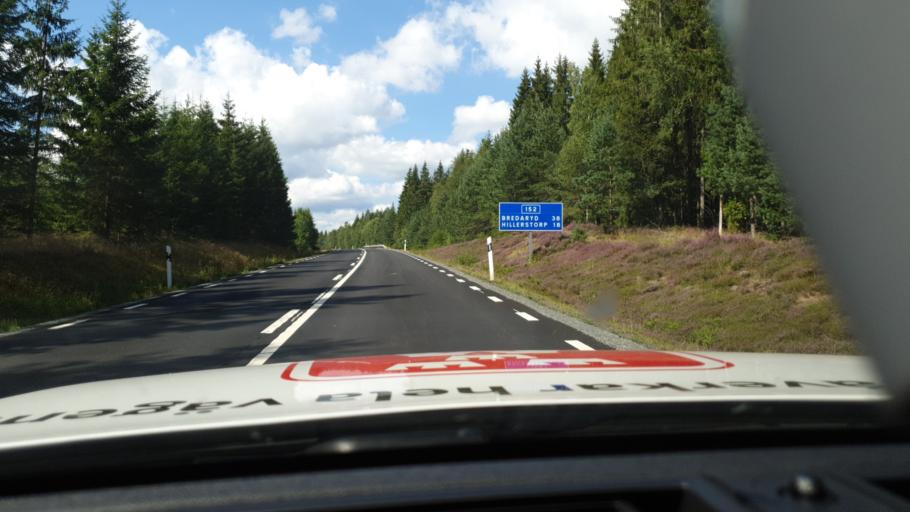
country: SE
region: Joenkoeping
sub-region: Vaggeryds Kommun
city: Skillingaryd
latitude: 57.4165
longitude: 14.0914
